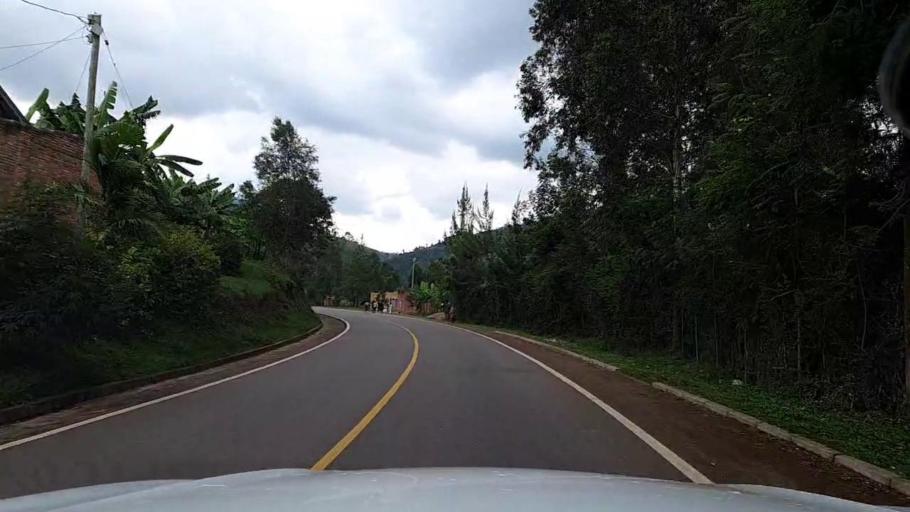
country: RW
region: Northern Province
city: Byumba
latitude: -1.6777
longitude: 30.0996
